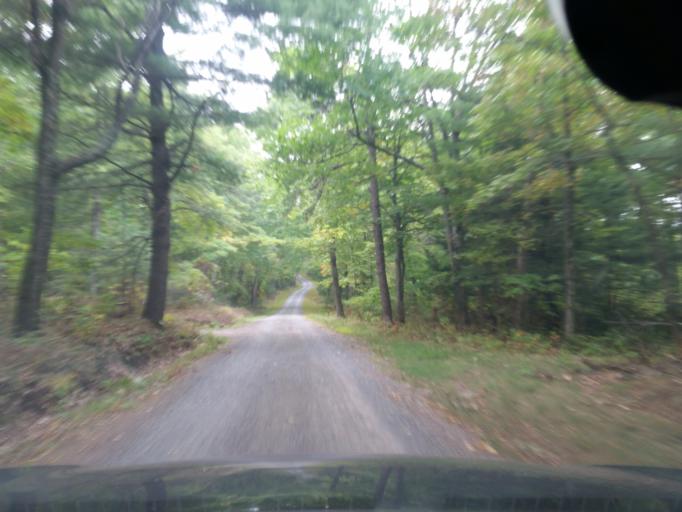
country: US
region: Pennsylvania
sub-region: Lycoming County
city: Jersey Shore
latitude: 41.0852
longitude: -77.1969
